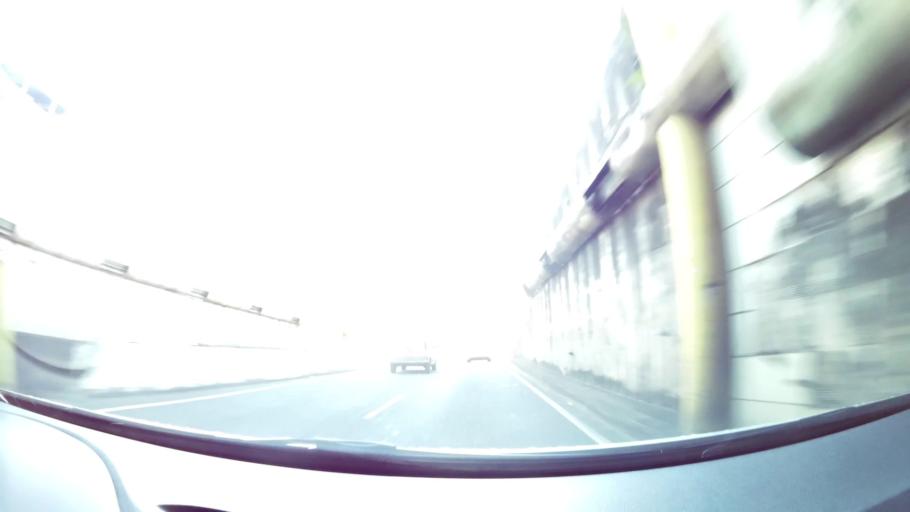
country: MQ
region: Martinique
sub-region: Martinique
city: Fort-de-France
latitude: 14.6152
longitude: -61.0617
